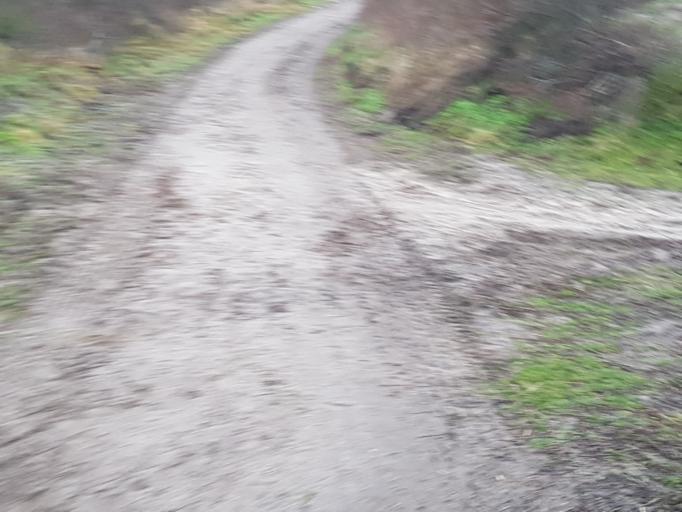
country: NL
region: North Holland
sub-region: Gemeente Bergen
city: Egmond aan Zee
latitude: 52.6335
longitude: 4.6301
